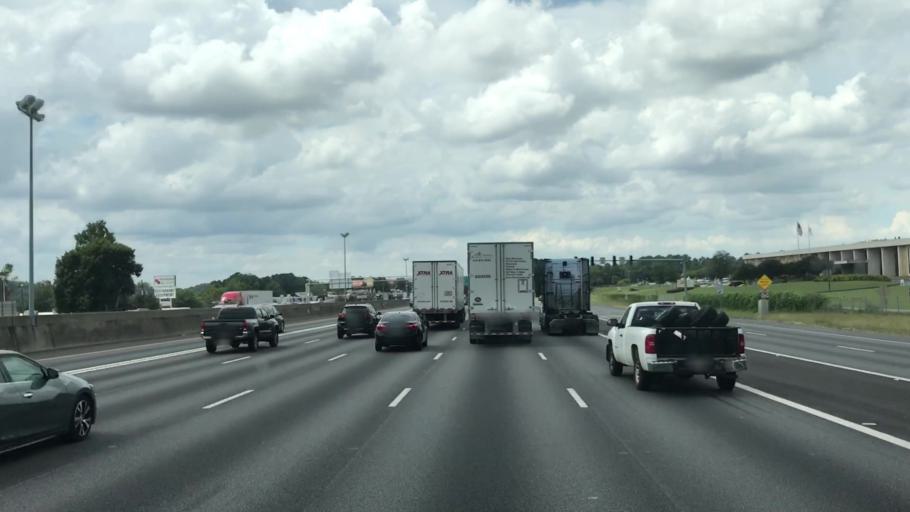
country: US
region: Georgia
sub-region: Gwinnett County
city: Norcross
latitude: 33.9123
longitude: -84.2114
